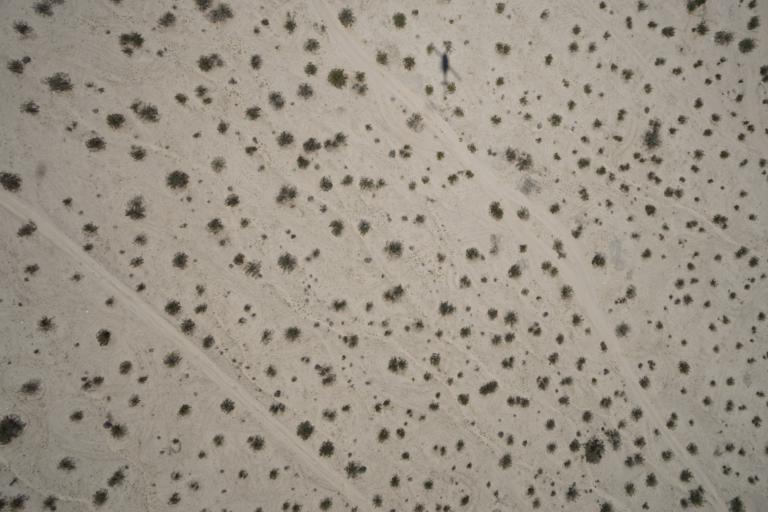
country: US
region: California
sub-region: San Bernardino County
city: Twentynine Palms
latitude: 34.1393
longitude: -116.0427
